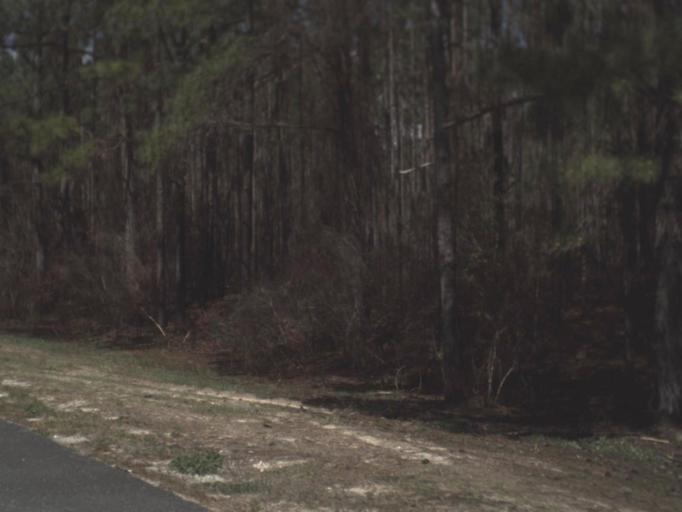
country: US
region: Florida
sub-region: Gadsden County
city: Midway
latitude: 30.3849
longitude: -84.5704
